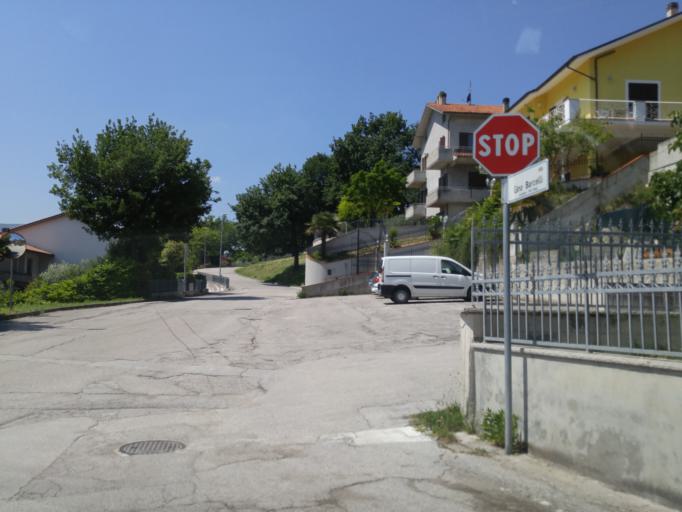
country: IT
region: The Marches
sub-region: Provincia di Pesaro e Urbino
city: Fossombrone
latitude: 43.6942
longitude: 12.8152
